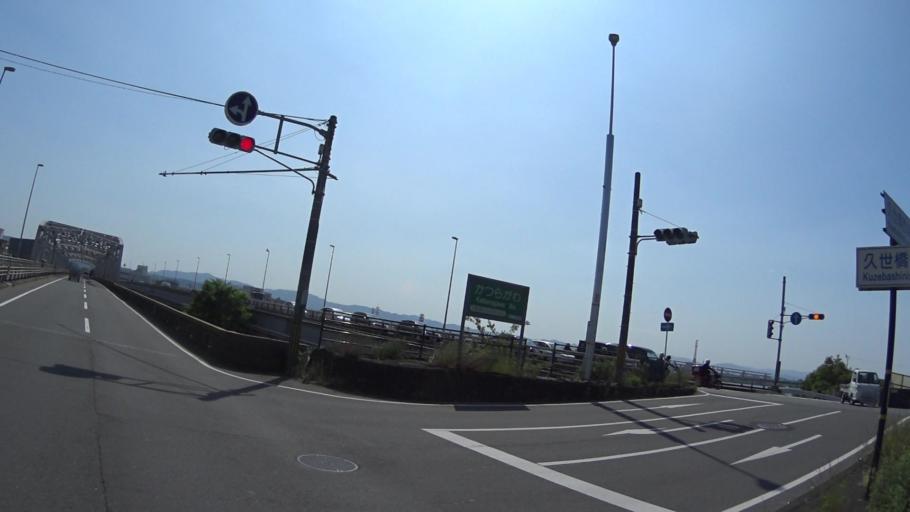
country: JP
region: Kyoto
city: Muko
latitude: 34.9655
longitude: 135.7209
